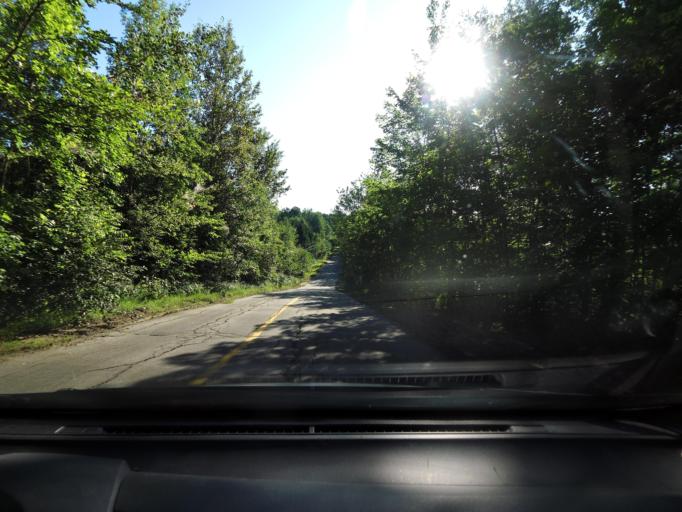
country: CA
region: Quebec
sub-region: Mauricie
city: Becancour
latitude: 46.5515
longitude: -72.3914
